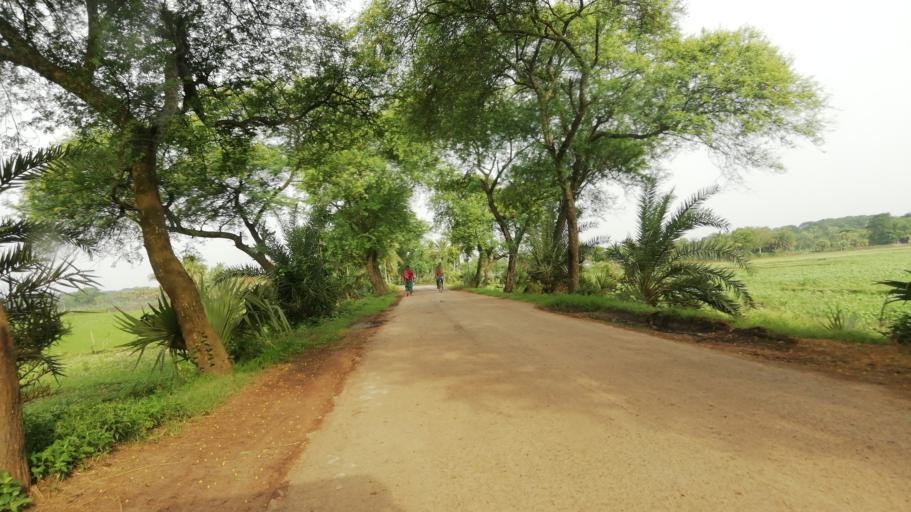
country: BD
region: Khulna
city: Bhatpara Abhaynagar
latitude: 23.0401
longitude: 89.3129
